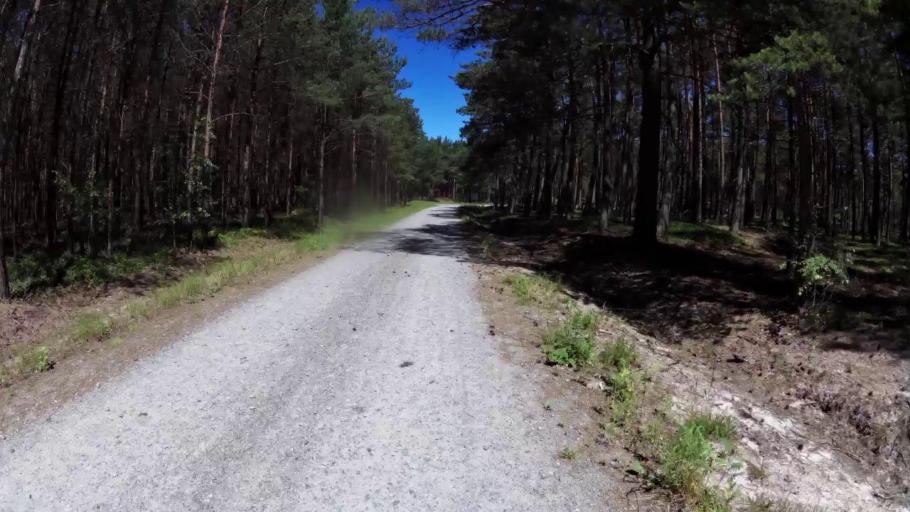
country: PL
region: West Pomeranian Voivodeship
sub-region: Powiat gryficki
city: Trzebiatow
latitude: 54.1034
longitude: 15.1730
